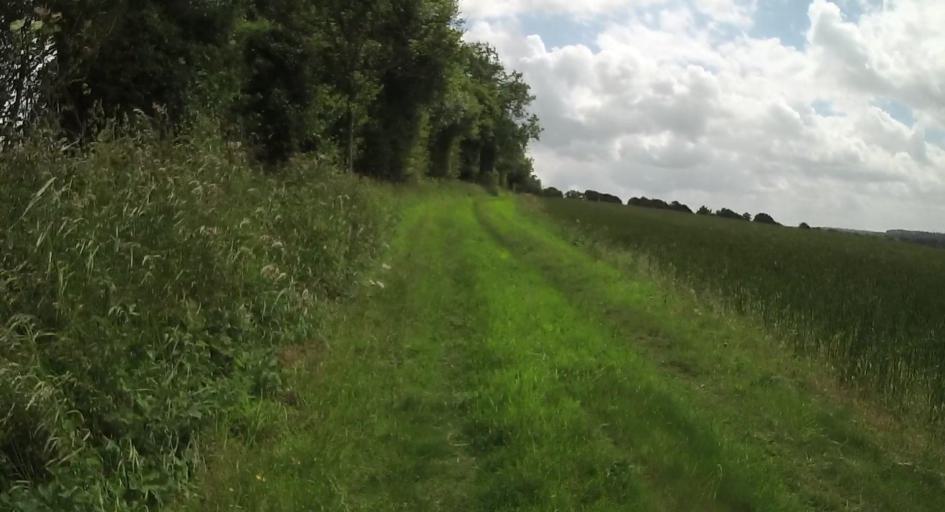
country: GB
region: England
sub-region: Hampshire
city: Basingstoke
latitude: 51.1721
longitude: -1.1652
